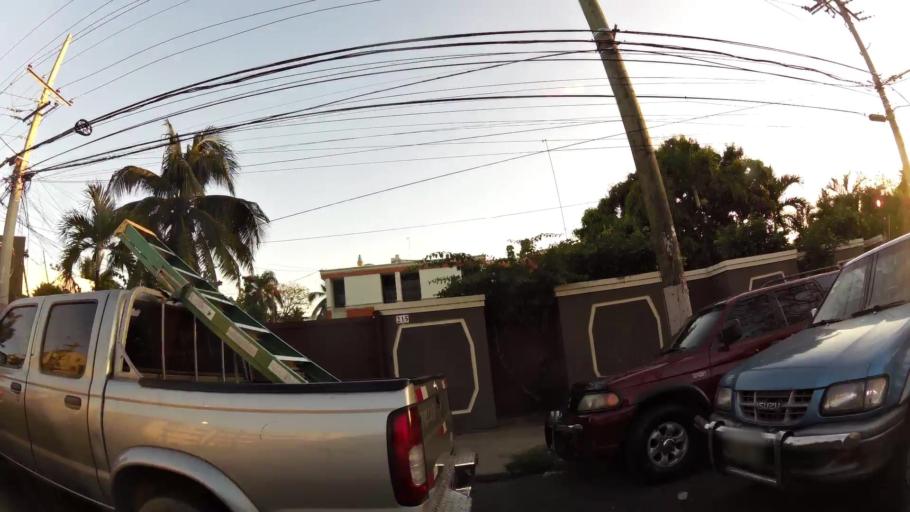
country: DO
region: Nacional
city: La Agustina
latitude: 18.5008
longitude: -69.9600
